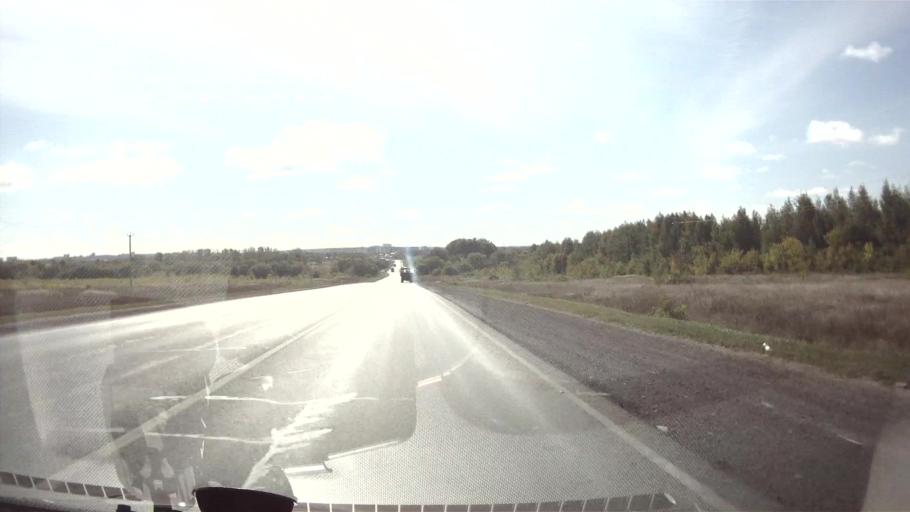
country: RU
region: Ulyanovsk
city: Isheyevka
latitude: 54.3089
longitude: 48.2380
